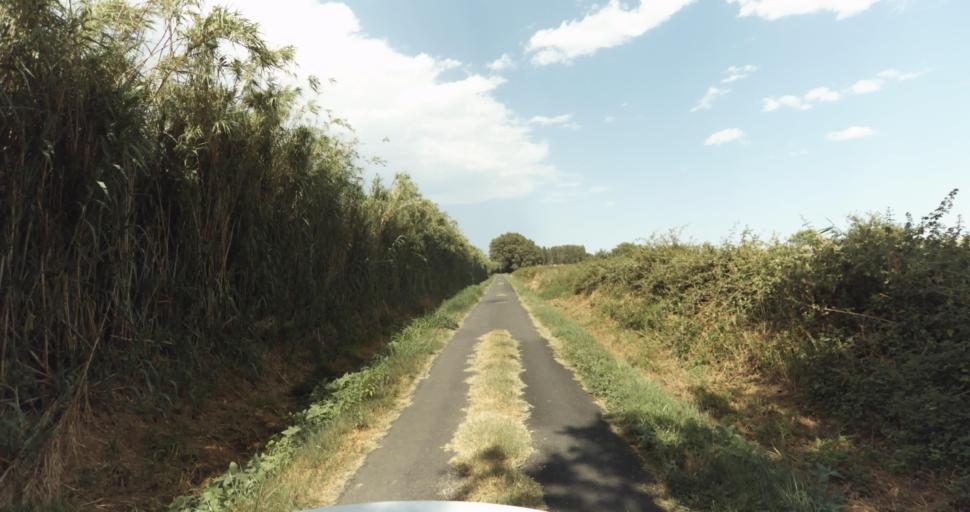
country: FR
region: Languedoc-Roussillon
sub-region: Departement des Pyrenees-Orientales
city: Alenya
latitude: 42.6292
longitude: 3.0011
